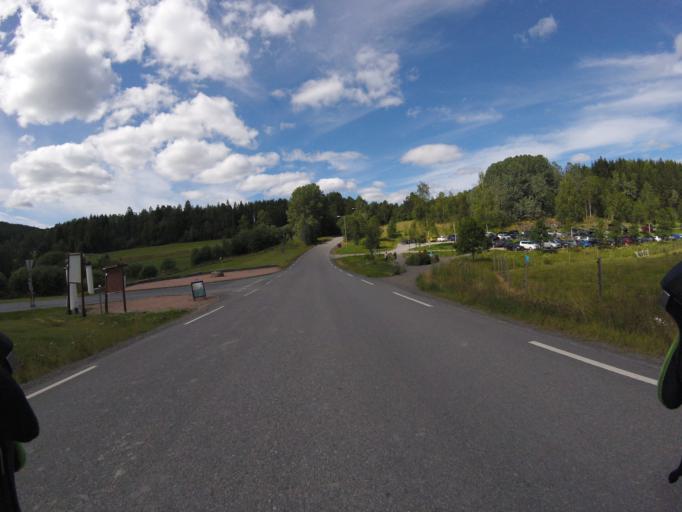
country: NO
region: Akershus
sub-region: Lorenskog
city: Kjenn
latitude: 59.8906
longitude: 10.9807
